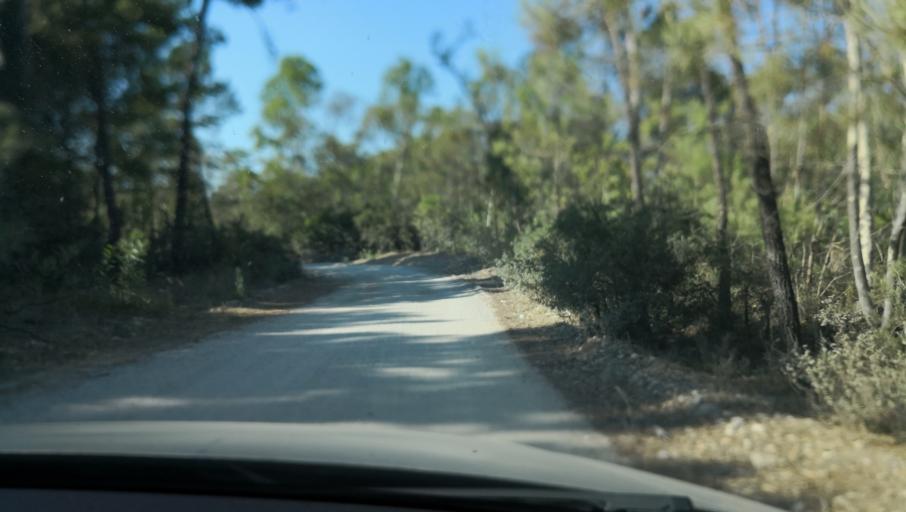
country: PT
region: Setubal
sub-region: Setubal
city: Setubal
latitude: 38.4696
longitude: -8.8759
